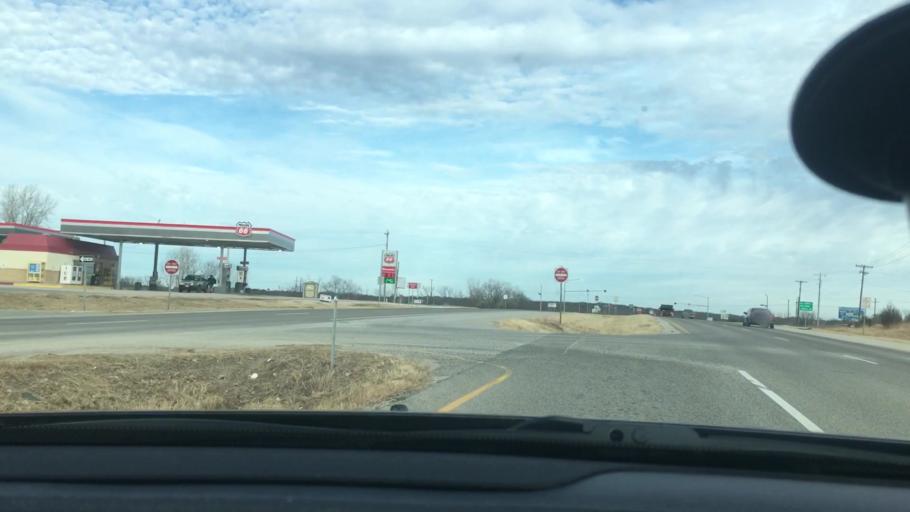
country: US
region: Oklahoma
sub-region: Seminole County
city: Konawa
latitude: 34.9391
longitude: -96.6830
